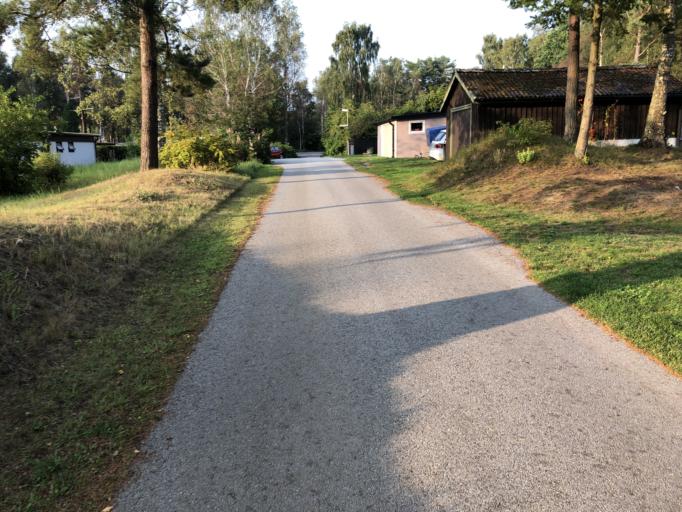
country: SE
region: Skane
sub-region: Ystads Kommun
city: Kopingebro
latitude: 55.4307
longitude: 13.9508
